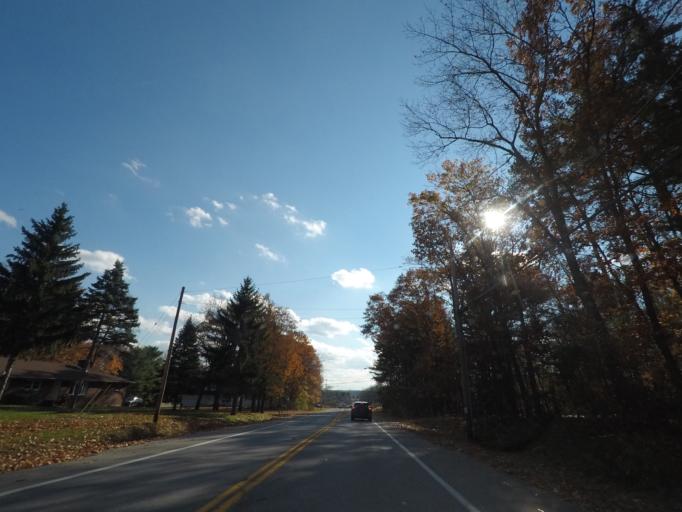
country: US
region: New York
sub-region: Schenectady County
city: East Glenville
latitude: 42.8680
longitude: -73.8879
